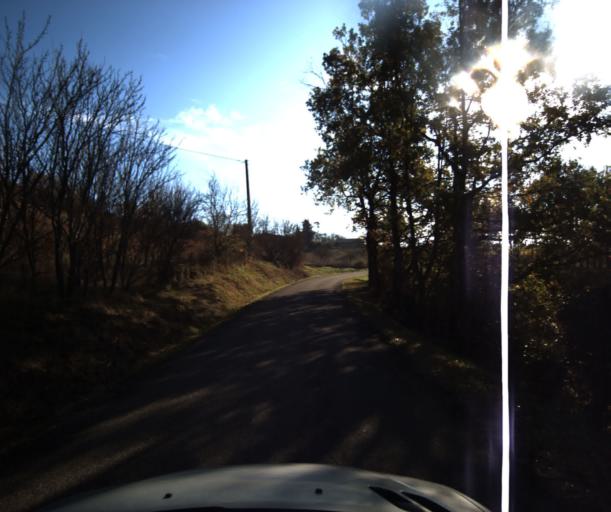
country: FR
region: Midi-Pyrenees
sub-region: Departement du Tarn-et-Garonne
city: Lafrancaise
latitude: 44.1107
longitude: 1.2902
